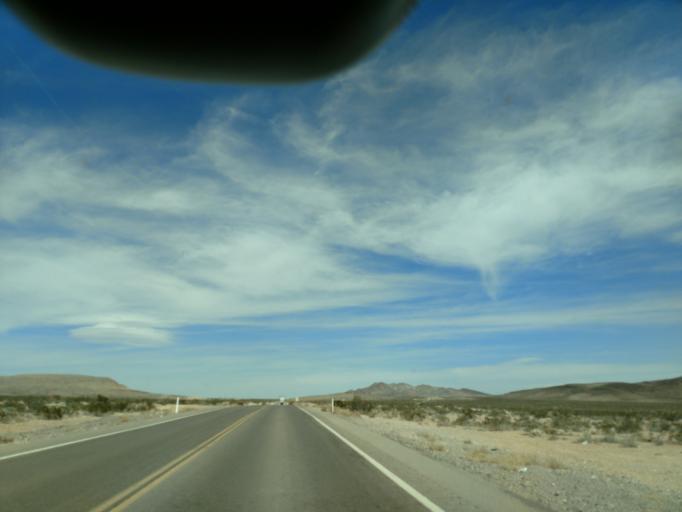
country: US
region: Nevada
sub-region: Clark County
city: Enterprise
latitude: 35.8512
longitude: -115.2600
